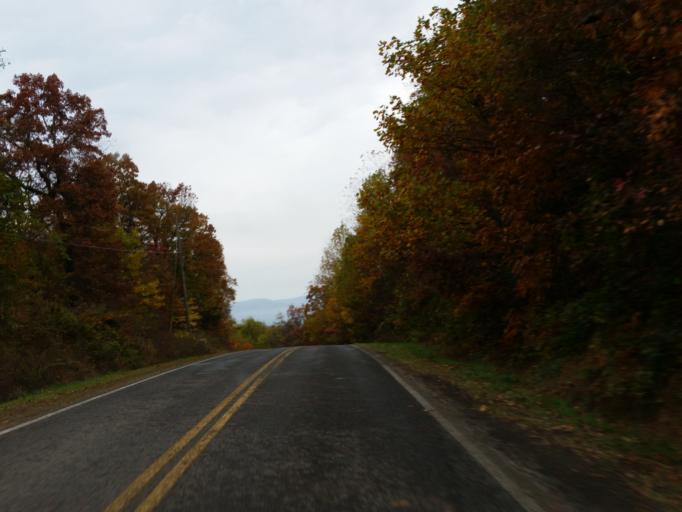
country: US
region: Georgia
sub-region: Pickens County
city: Jasper
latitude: 34.5449
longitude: -84.3474
